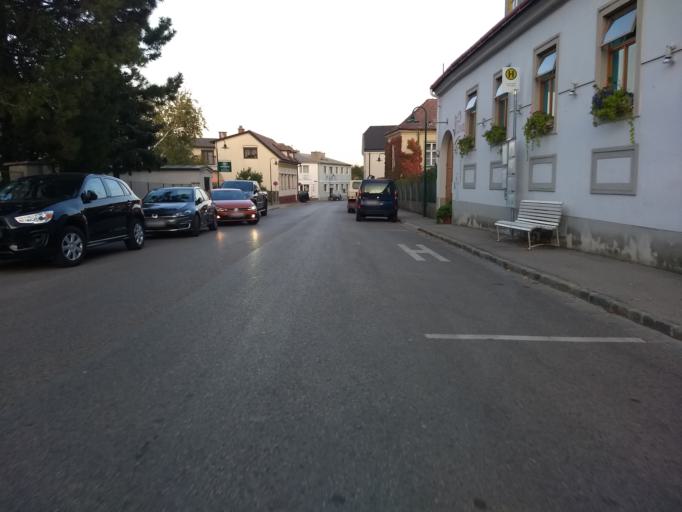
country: AT
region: Lower Austria
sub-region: Politischer Bezirk Modling
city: Perchtoldsdorf
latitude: 48.1222
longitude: 16.2609
